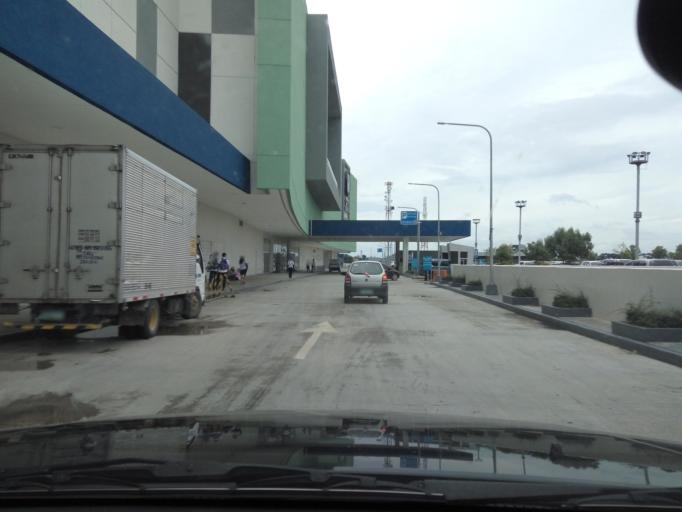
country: PH
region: Central Luzon
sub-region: Province of Nueva Ecija
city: Cabanatuan City
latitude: 15.4658
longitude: 120.9551
